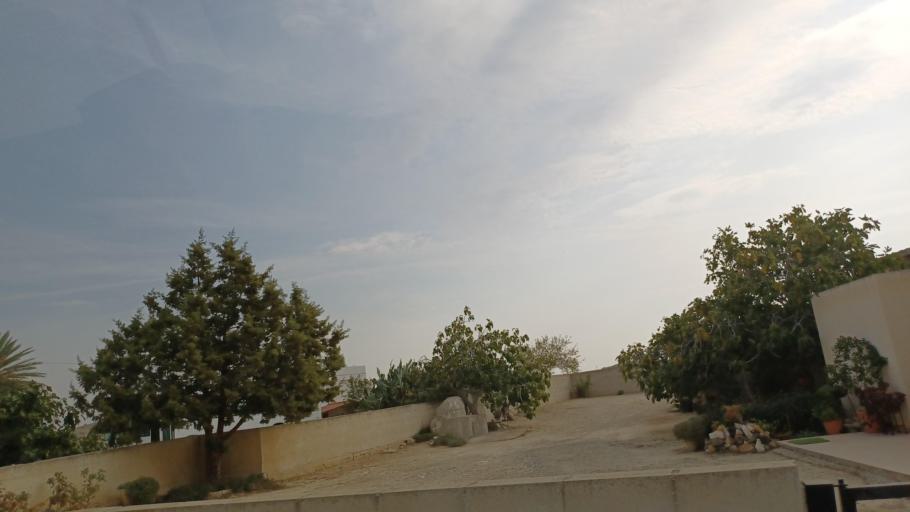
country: CY
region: Larnaka
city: Troulloi
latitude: 35.0095
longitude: 33.5699
